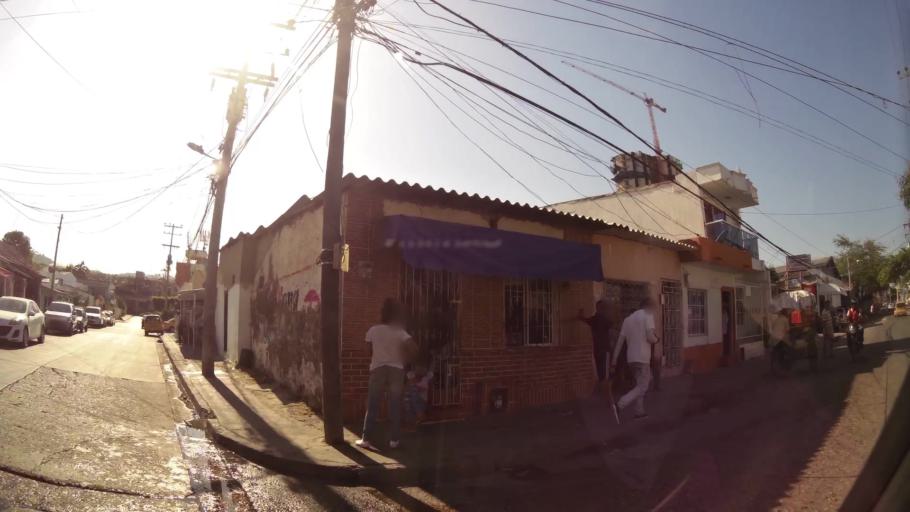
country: CO
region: Bolivar
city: Cartagena
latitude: 10.4274
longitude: -75.5378
